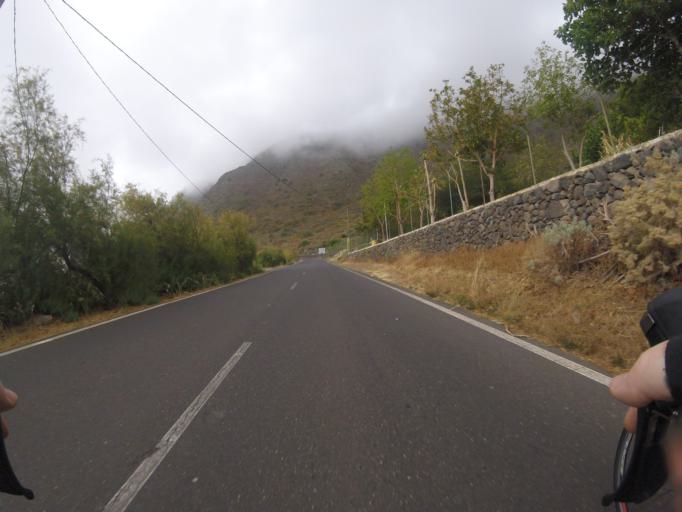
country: ES
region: Canary Islands
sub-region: Provincia de Santa Cruz de Tenerife
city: Guimar
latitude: 28.2976
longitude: -16.4178
